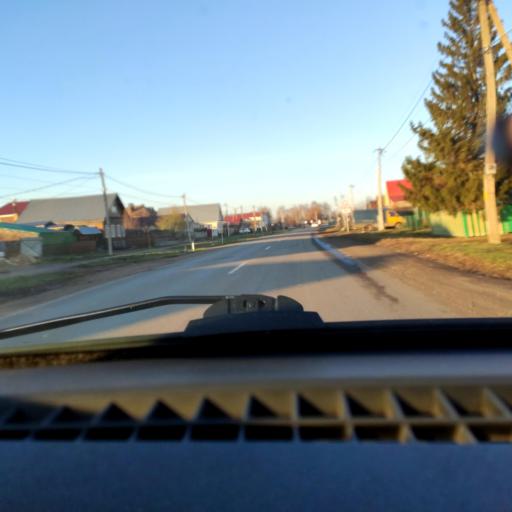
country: RU
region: Bashkortostan
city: Ufa
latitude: 54.6126
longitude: 55.9009
